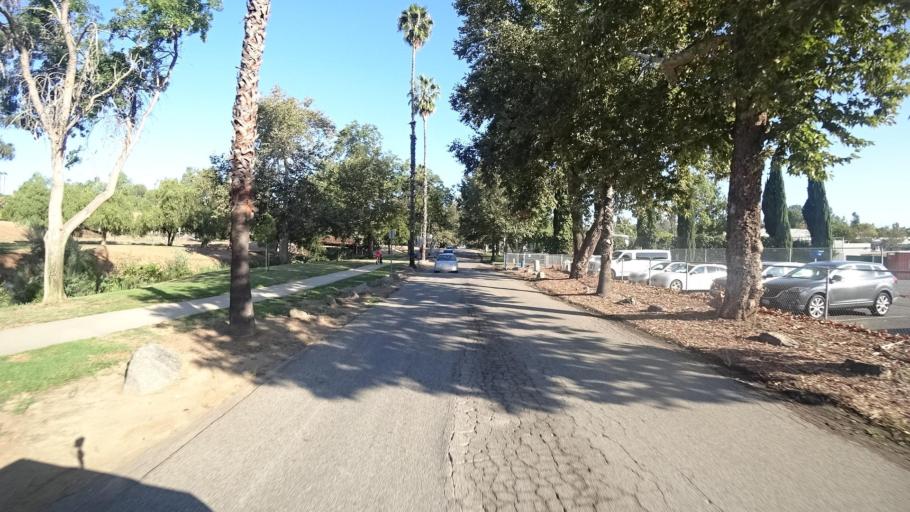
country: US
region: California
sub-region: San Diego County
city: Escondido
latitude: 33.0842
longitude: -117.0610
